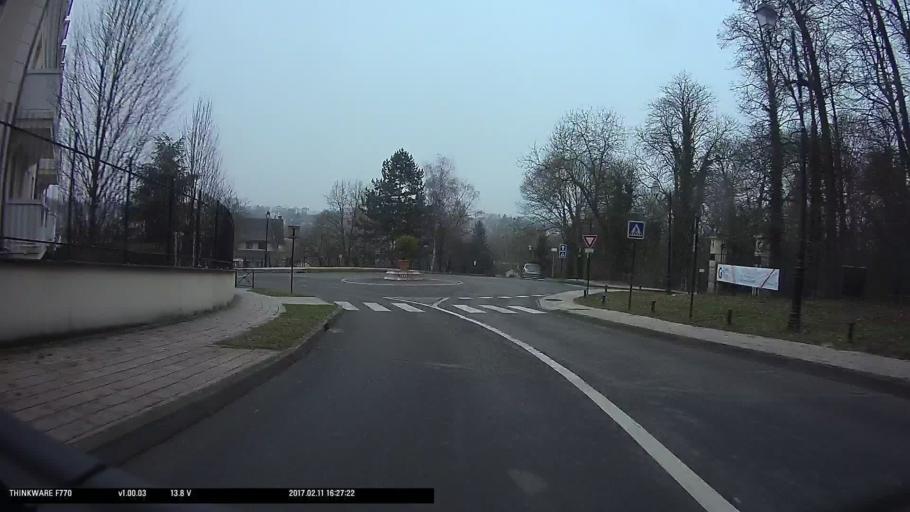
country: FR
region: Ile-de-France
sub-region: Departement du Val-d'Oise
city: Osny
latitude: 49.0637
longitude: 2.0647
